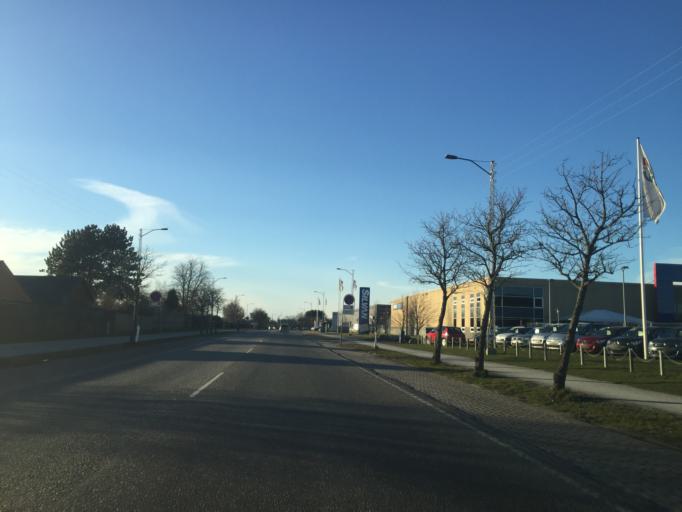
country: DK
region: Capital Region
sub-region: Tarnby Kommune
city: Tarnby
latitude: 55.6150
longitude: 12.6101
